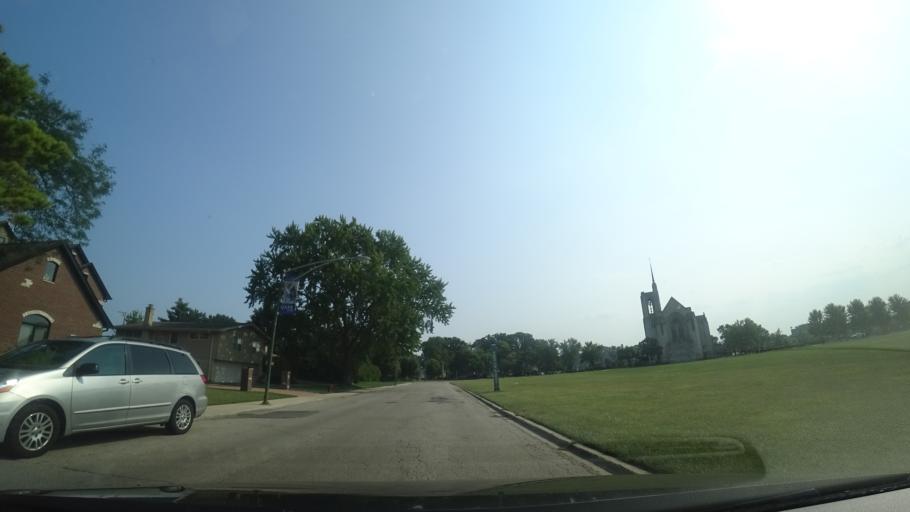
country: US
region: Illinois
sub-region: Cook County
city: Lincolnwood
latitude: 41.9965
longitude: -87.7435
